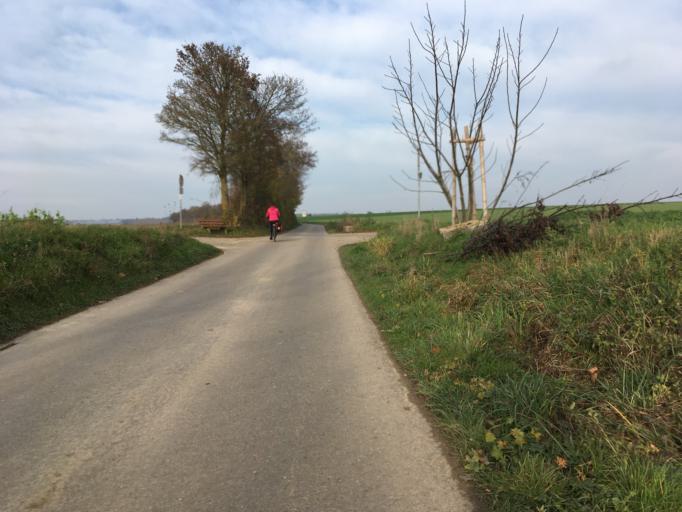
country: DE
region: Baden-Wuerttemberg
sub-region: Regierungsbezirk Stuttgart
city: Offenau
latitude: 49.2541
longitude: 9.1368
